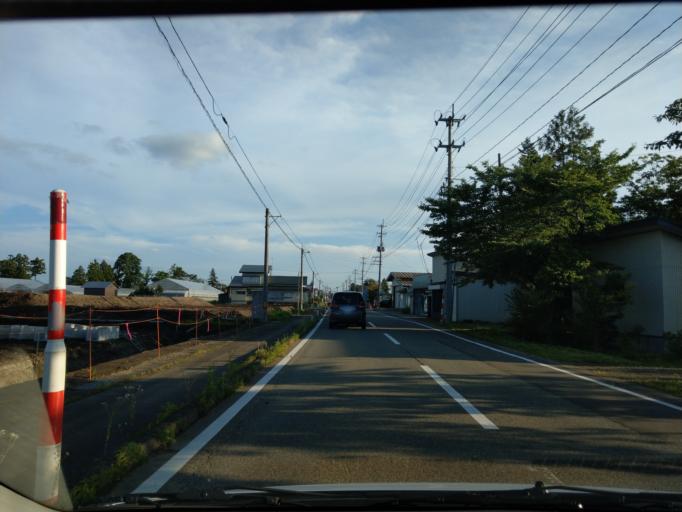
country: JP
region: Akita
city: Omagari
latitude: 39.4460
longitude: 140.5670
